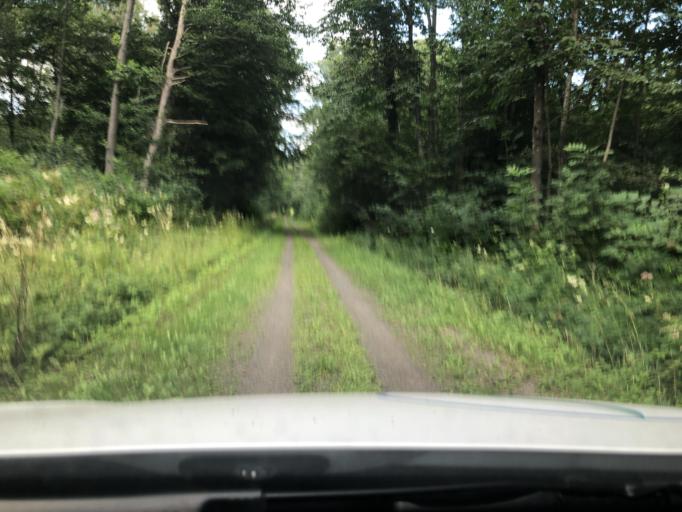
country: SE
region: Skane
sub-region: Kristianstads Kommun
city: Degeberga
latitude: 55.7779
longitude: 14.1695
